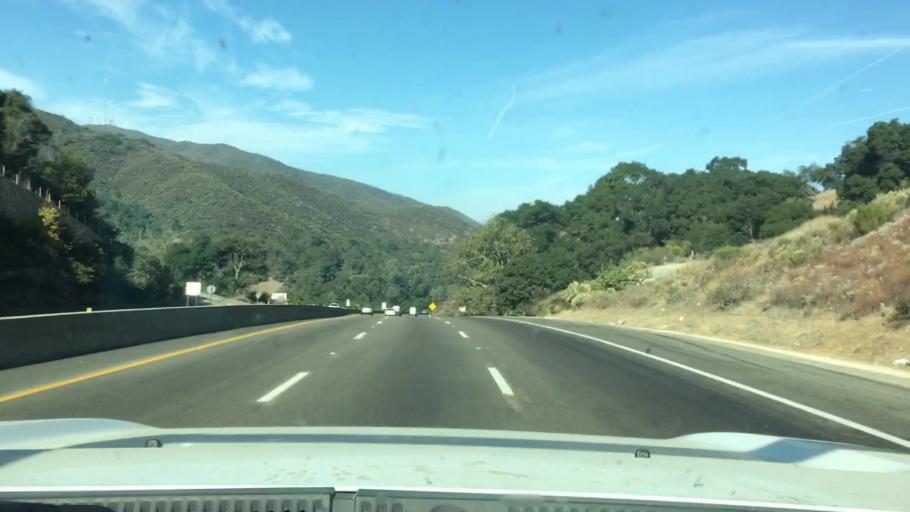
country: US
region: California
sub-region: San Luis Obispo County
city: Santa Margarita
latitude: 35.3493
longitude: -120.6311
